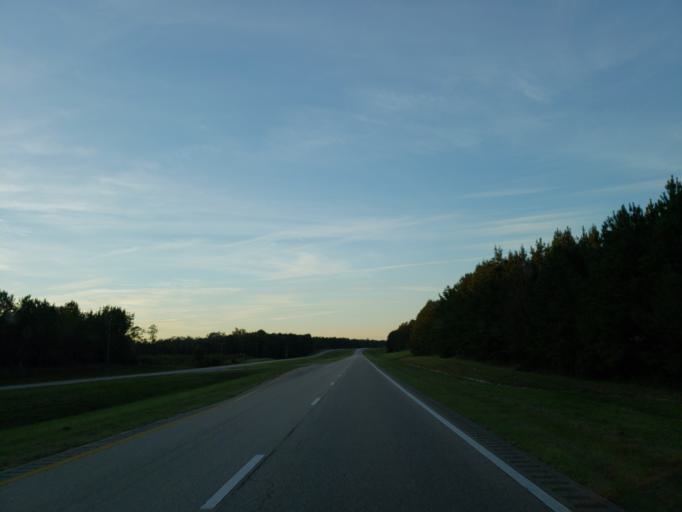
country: US
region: Mississippi
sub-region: Wayne County
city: Belmont
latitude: 31.4837
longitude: -88.4860
